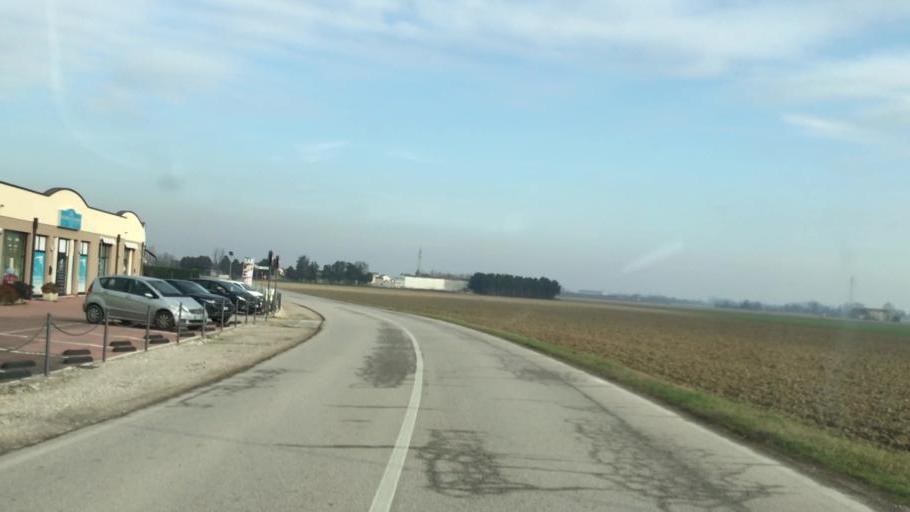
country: IT
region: Veneto
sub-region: Provincia di Rovigo
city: Fratta Polesine
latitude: 45.0305
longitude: 11.6495
